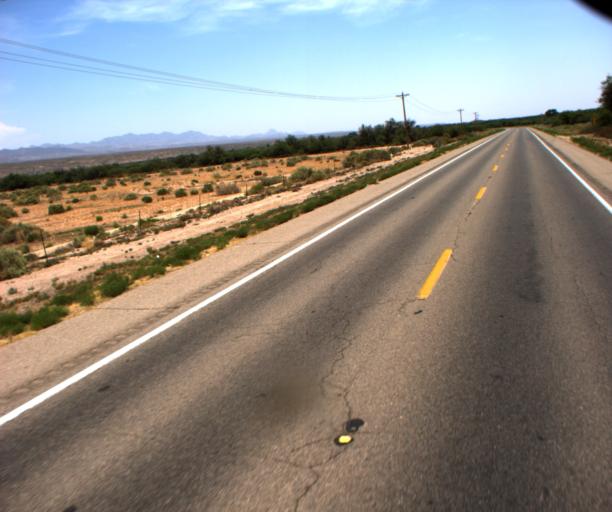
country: US
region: Arizona
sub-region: Graham County
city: Bylas
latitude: 33.0450
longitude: -109.9828
